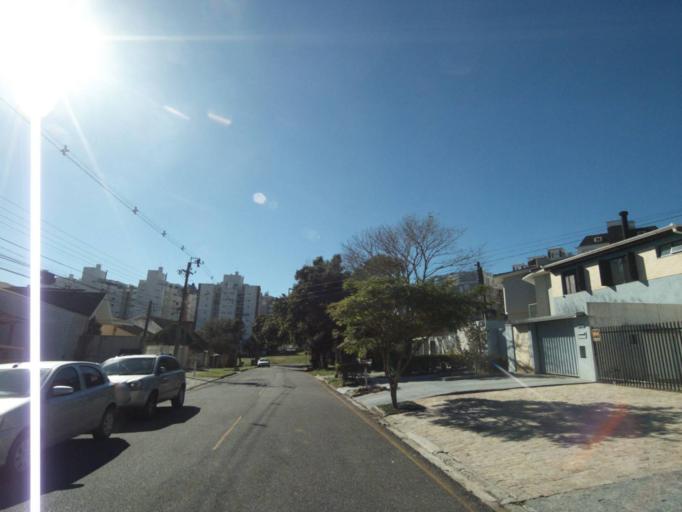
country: BR
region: Parana
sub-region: Curitiba
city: Curitiba
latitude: -25.4135
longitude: -49.2433
